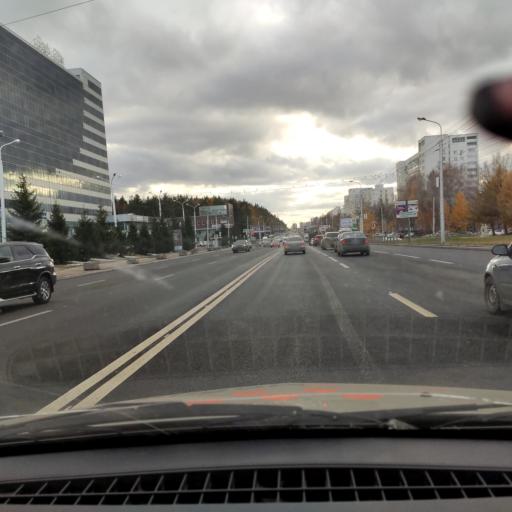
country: RU
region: Bashkortostan
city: Ufa
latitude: 54.7515
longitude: 56.0317
